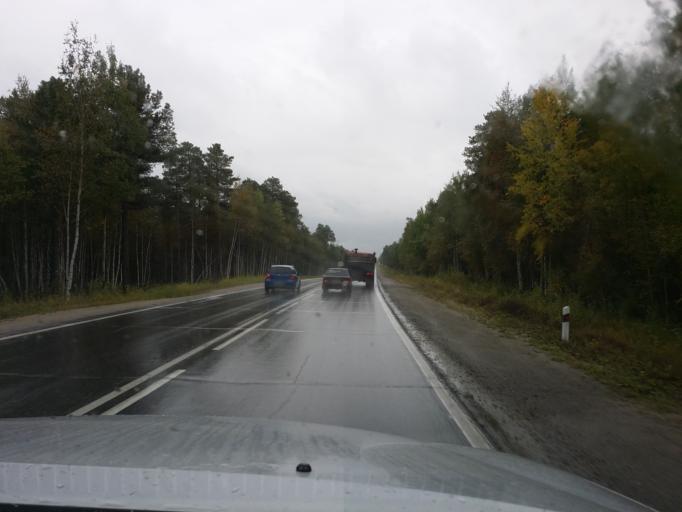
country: RU
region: Khanty-Mansiyskiy Avtonomnyy Okrug
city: Megion
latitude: 61.1574
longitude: 75.7330
